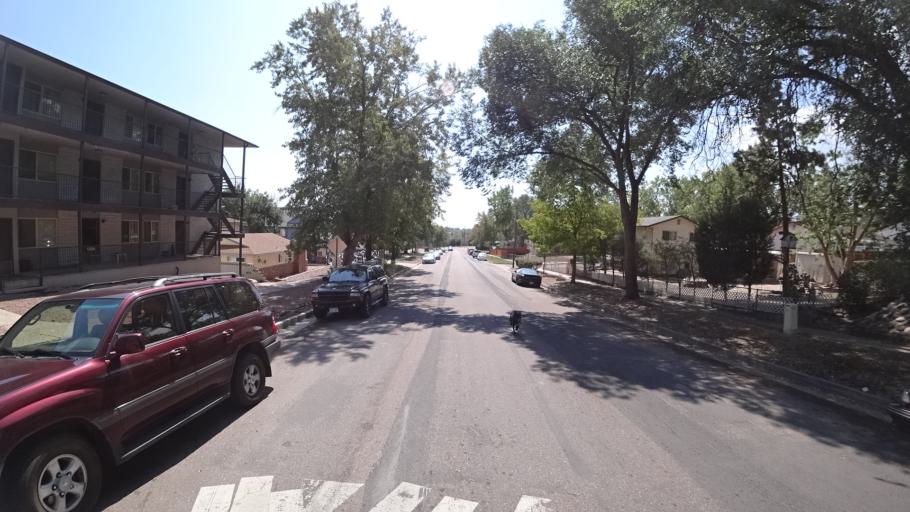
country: US
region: Colorado
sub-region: El Paso County
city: Stratmoor
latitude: 38.8273
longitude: -104.7627
